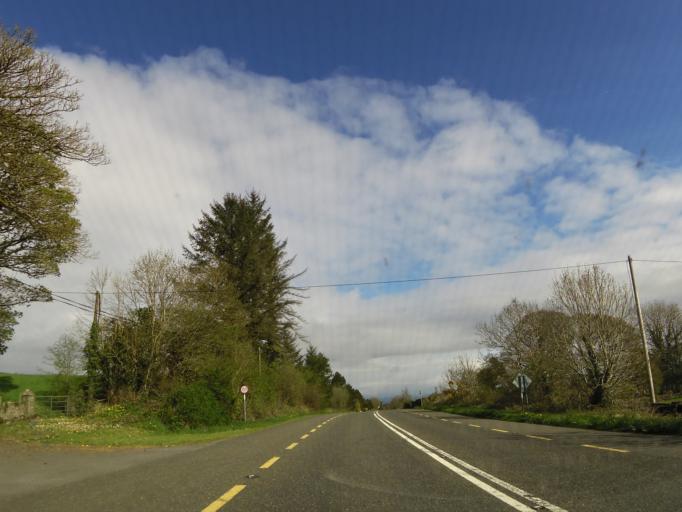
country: IE
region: Connaught
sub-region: Sligo
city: Tobercurry
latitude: 53.9286
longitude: -8.7849
